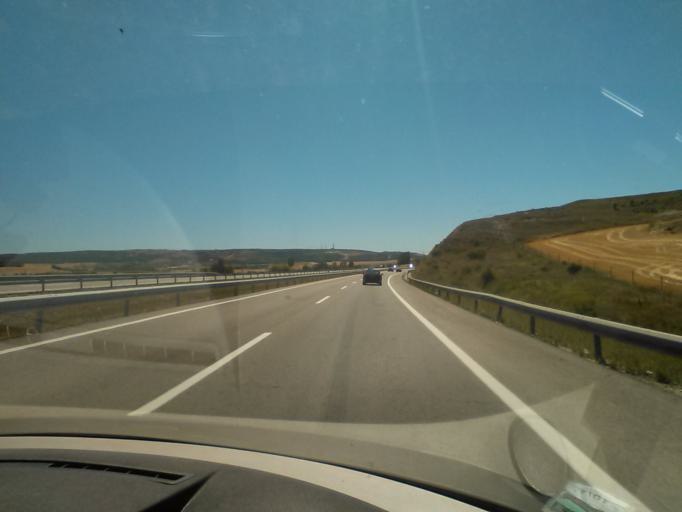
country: ES
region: Castille and Leon
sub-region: Provincia de Burgos
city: Quintanapalla
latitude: 42.4187
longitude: -3.5213
